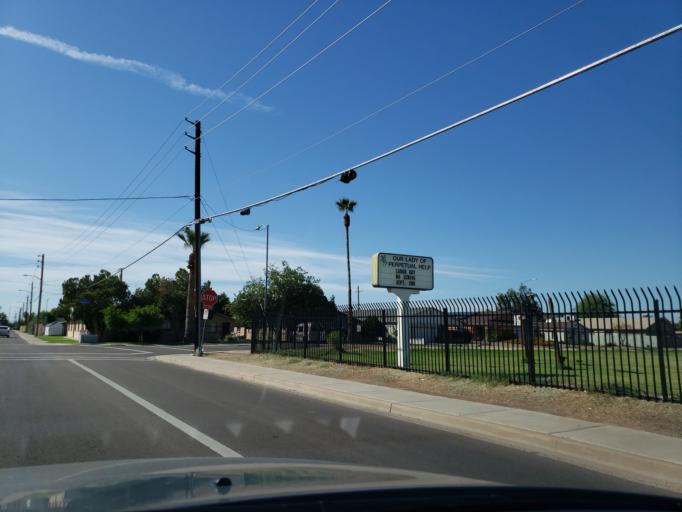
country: US
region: Arizona
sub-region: Maricopa County
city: Glendale
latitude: 33.5461
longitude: -112.1775
